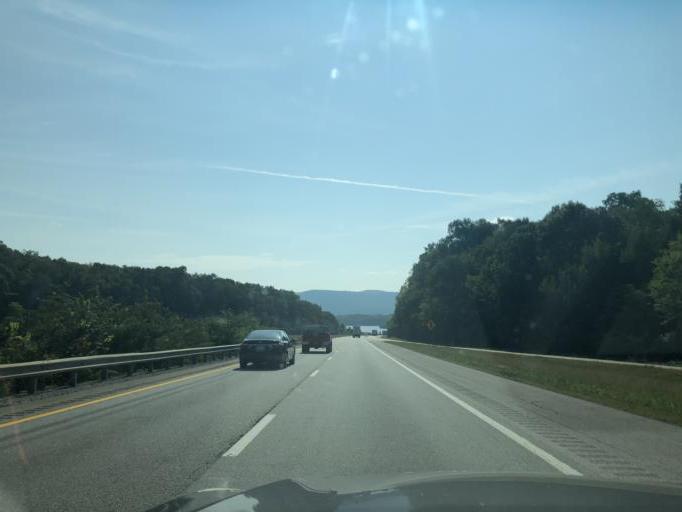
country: US
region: Tennessee
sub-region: Marion County
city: Jasper
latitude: 35.0316
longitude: -85.5812
